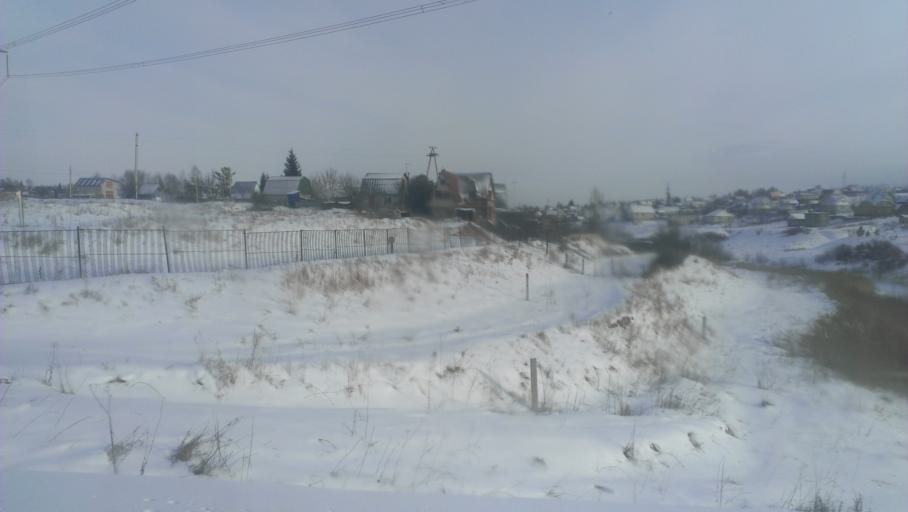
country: RU
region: Altai Krai
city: Gon'ba
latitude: 53.4158
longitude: 83.5503
